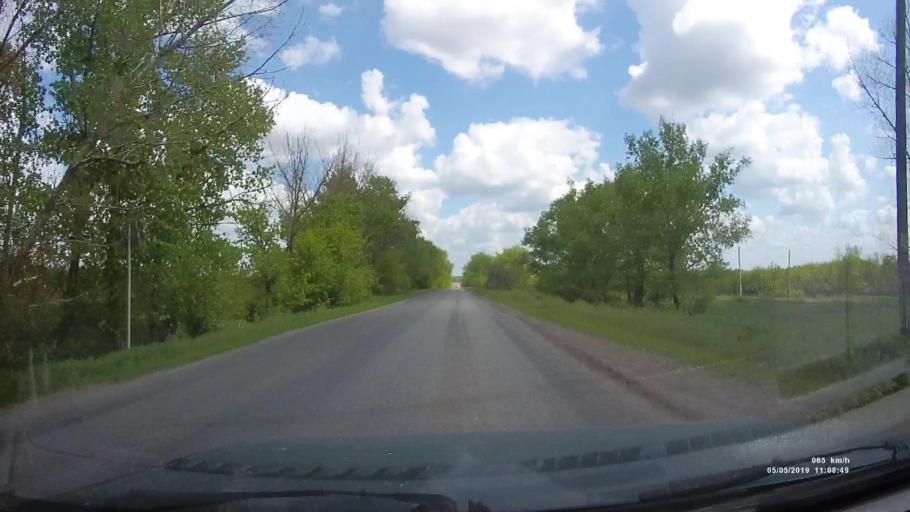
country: RU
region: Rostov
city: Ust'-Donetskiy
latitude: 47.7366
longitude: 40.9180
